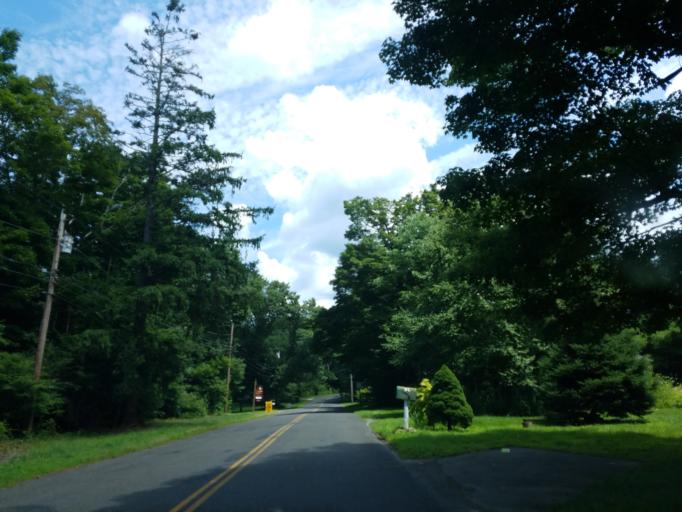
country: US
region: Connecticut
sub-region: Fairfield County
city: Trumbull
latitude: 41.2740
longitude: -73.2947
